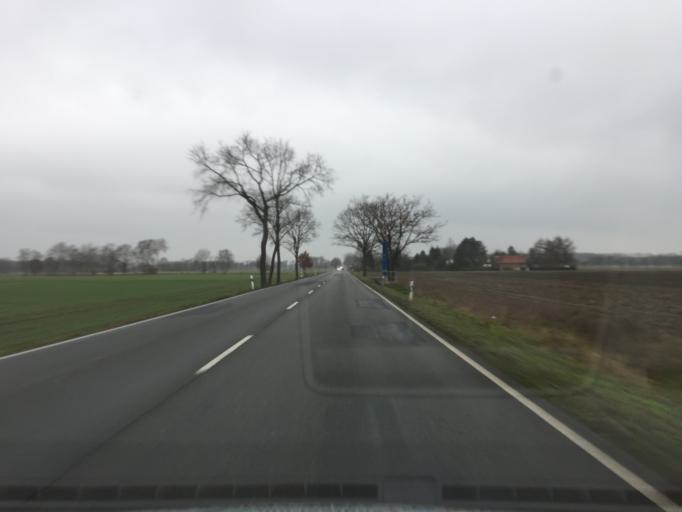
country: DE
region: Lower Saxony
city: Uchte
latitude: 52.5177
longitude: 8.8979
